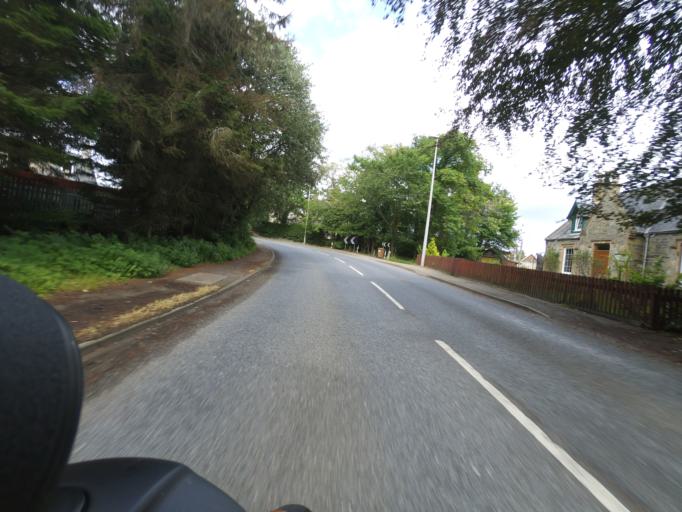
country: GB
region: Scotland
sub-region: Highland
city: Grantown on Spey
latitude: 57.3281
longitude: -3.6073
